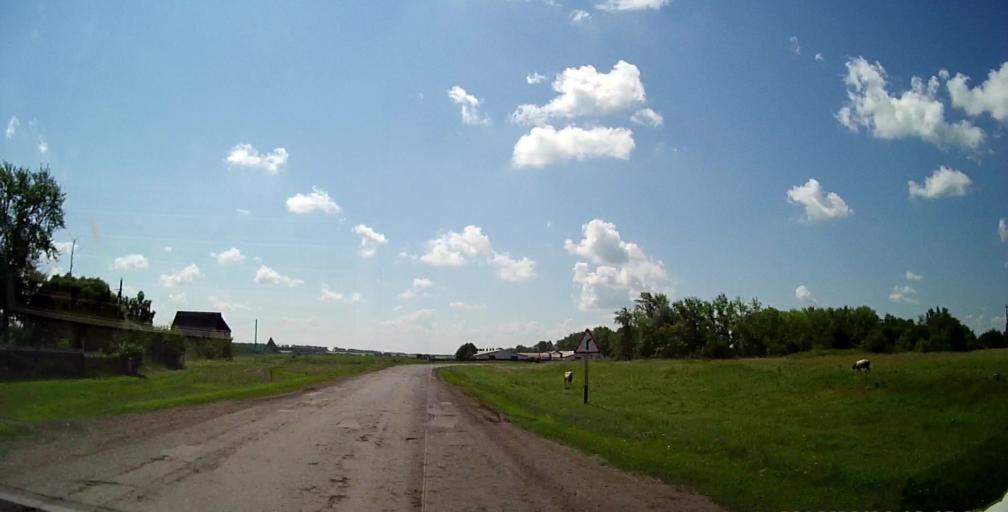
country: RU
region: Lipetsk
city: Chaplygin
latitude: 53.3173
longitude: 39.9594
